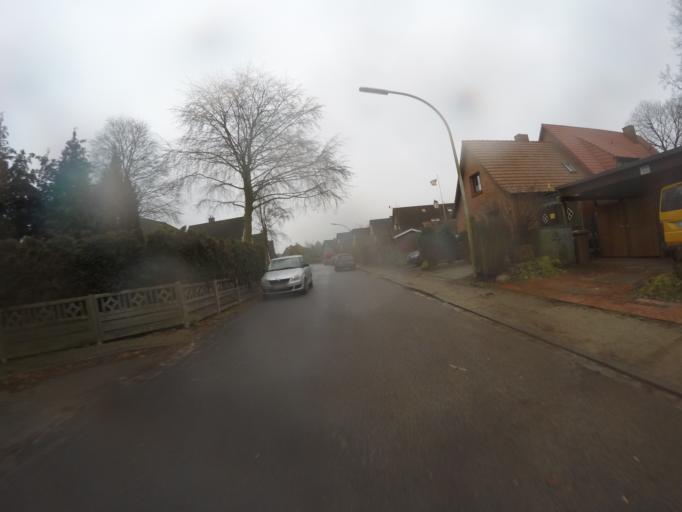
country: DE
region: Schleswig-Holstein
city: Quickborn
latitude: 53.7280
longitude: 9.9074
